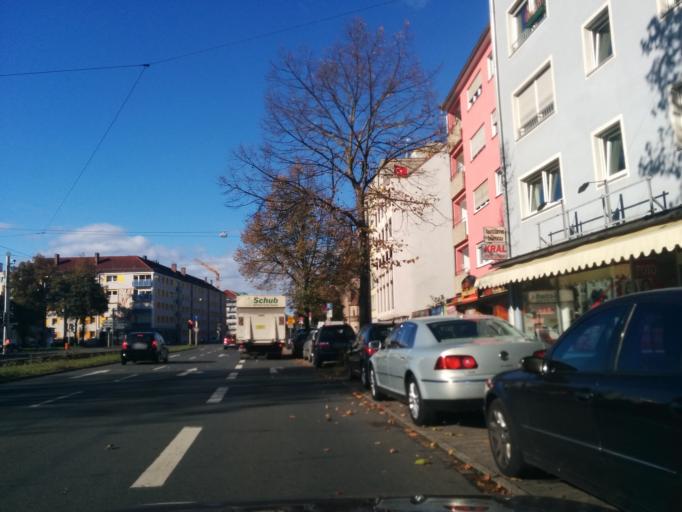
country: DE
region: Bavaria
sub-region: Regierungsbezirk Mittelfranken
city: Nuernberg
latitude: 49.4432
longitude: 11.1012
